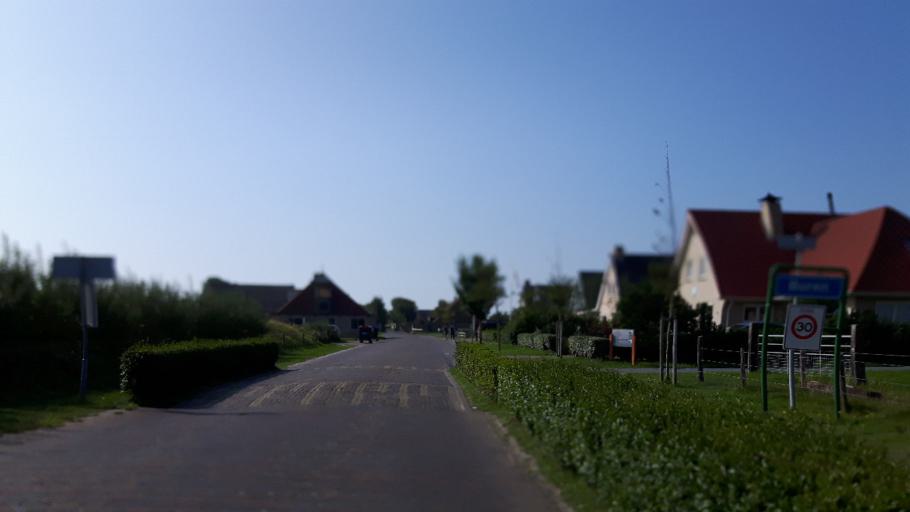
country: NL
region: Friesland
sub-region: Gemeente Ameland
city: Nes
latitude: 53.4515
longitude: 5.8014
